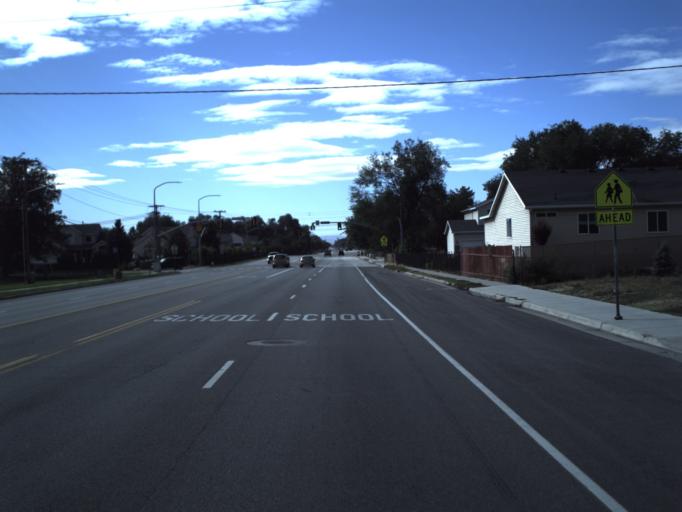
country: US
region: Utah
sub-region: Salt Lake County
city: Salt Lake City
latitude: 40.7923
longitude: -111.9393
